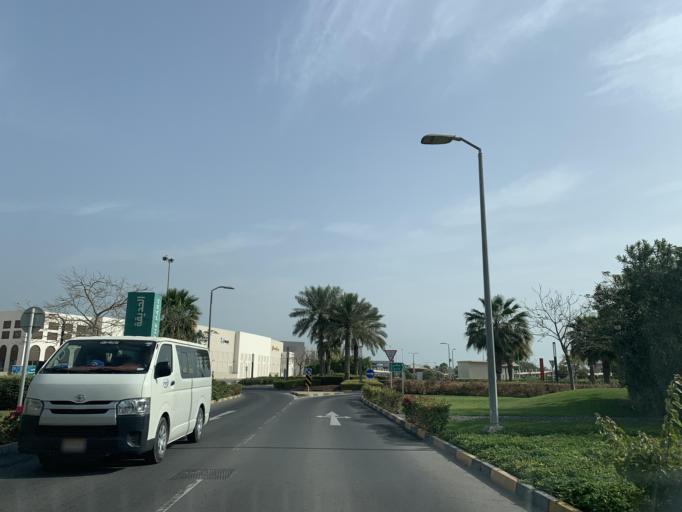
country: BH
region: Manama
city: Manama
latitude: 26.2430
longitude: 50.5842
